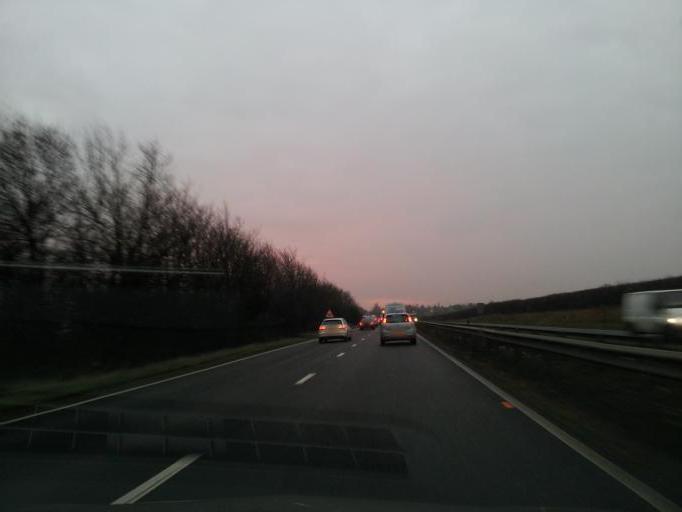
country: GB
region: England
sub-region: Peterborough
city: Wittering
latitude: 52.6196
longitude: -0.4526
